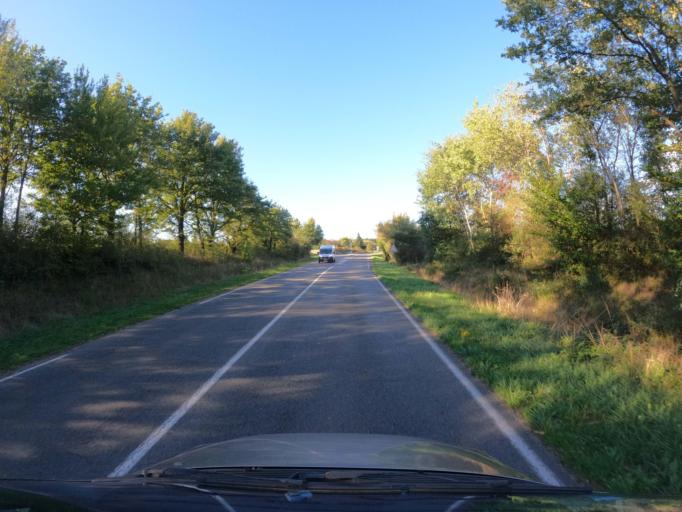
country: FR
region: Bourgogne
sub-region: Departement de Saone-et-Loire
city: Torcy
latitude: 46.7539
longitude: 4.4405
